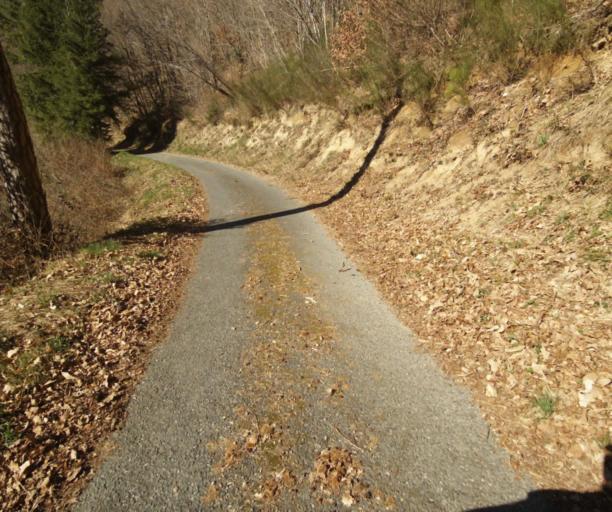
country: FR
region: Limousin
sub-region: Departement de la Correze
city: Tulle
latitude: 45.2718
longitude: 1.7435
